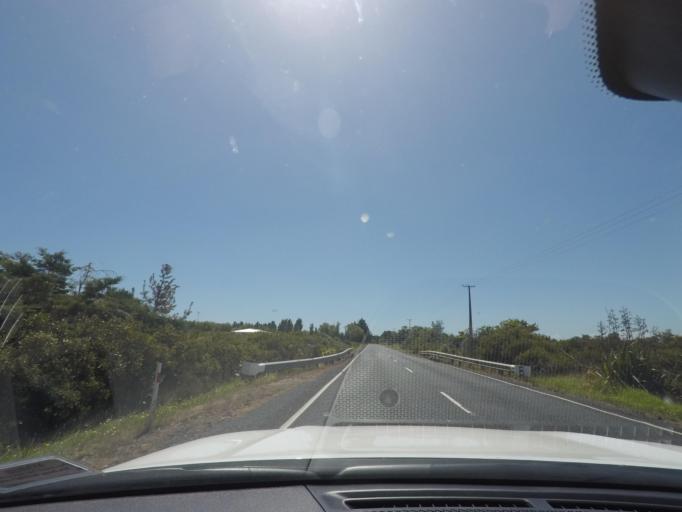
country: NZ
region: Auckland
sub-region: Auckland
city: Parakai
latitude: -36.6393
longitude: 174.3886
